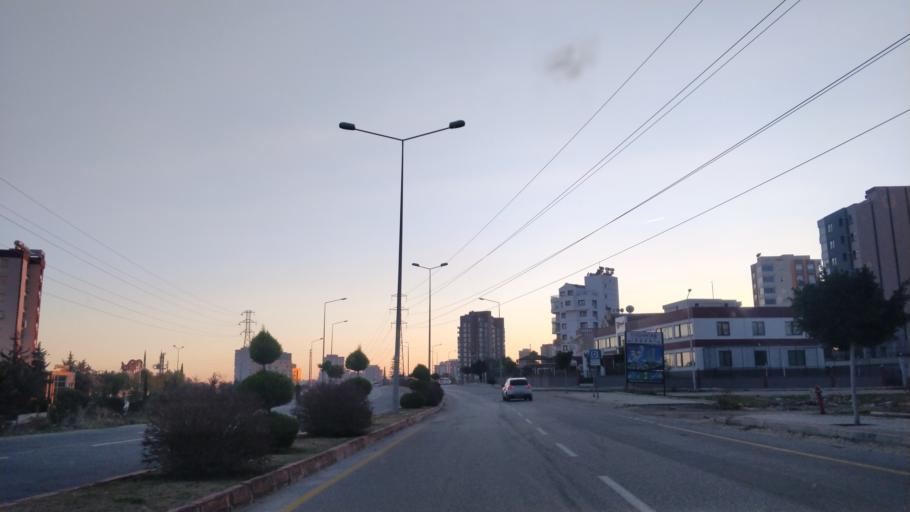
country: TR
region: Mersin
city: Mercin
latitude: 36.8042
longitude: 34.5715
